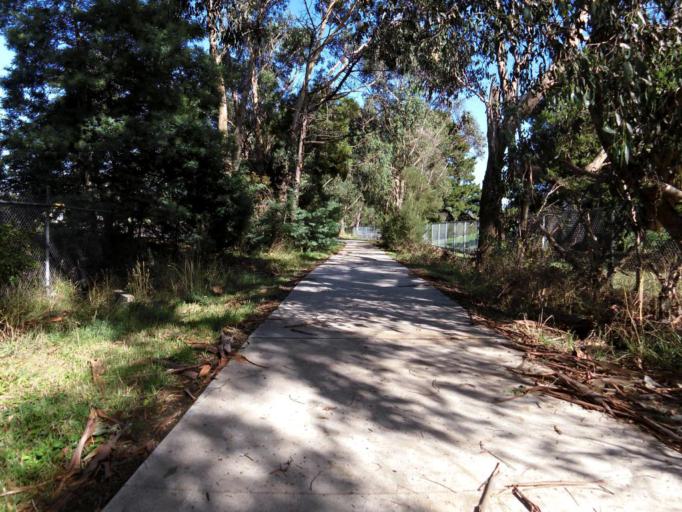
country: AU
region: Victoria
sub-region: Maroondah
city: Bayswater North
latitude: -37.8106
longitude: 145.2991
